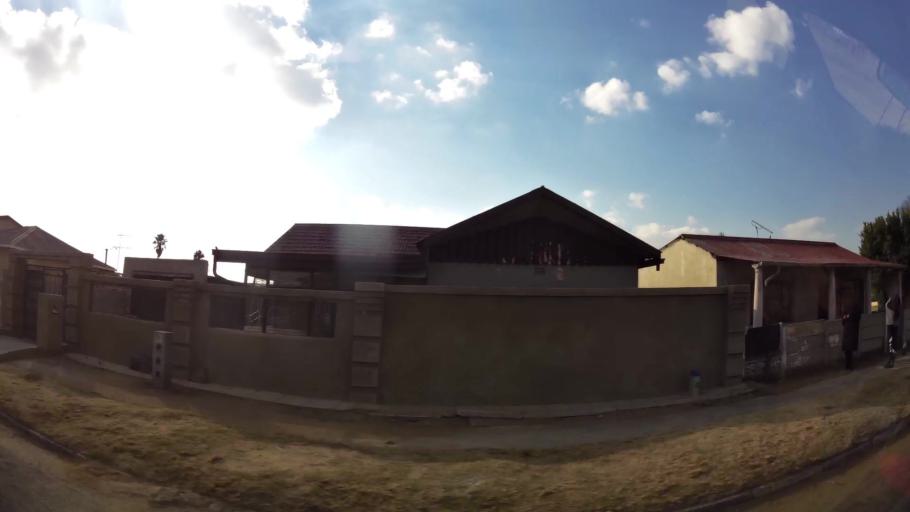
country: ZA
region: Gauteng
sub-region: West Rand District Municipality
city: Krugersdorp
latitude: -26.1010
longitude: 27.7523
